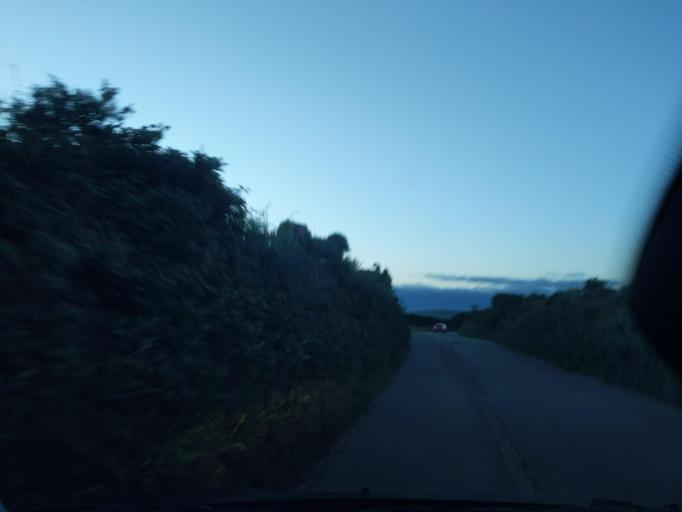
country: GB
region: England
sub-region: Cornwall
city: St. Buryan
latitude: 50.0571
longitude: -5.6371
